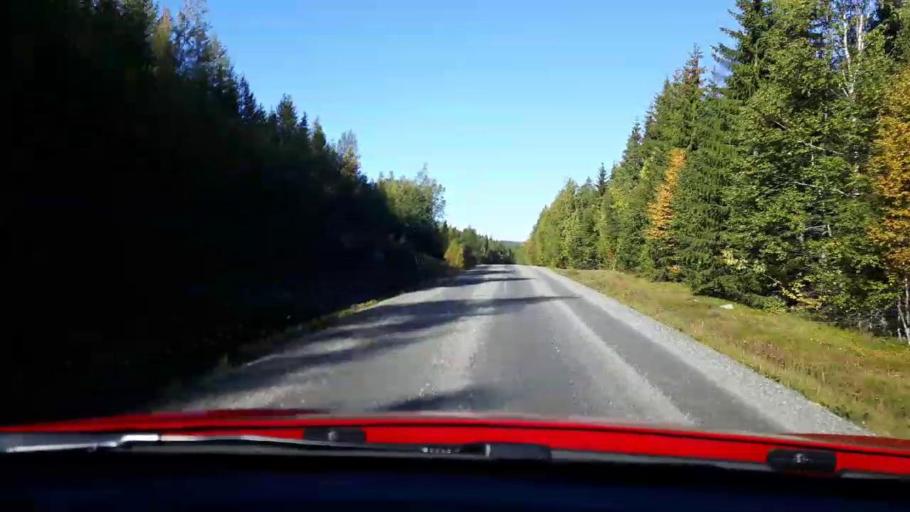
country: NO
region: Nord-Trondelag
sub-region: Lierne
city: Sandvika
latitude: 64.5237
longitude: 14.0732
